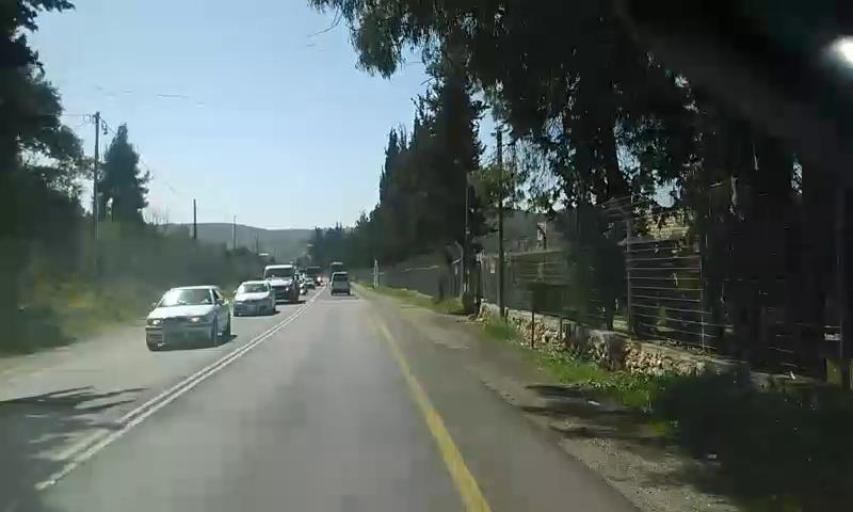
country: PS
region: West Bank
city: Shuyukh al `Arrub
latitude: 31.6325
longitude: 35.1320
